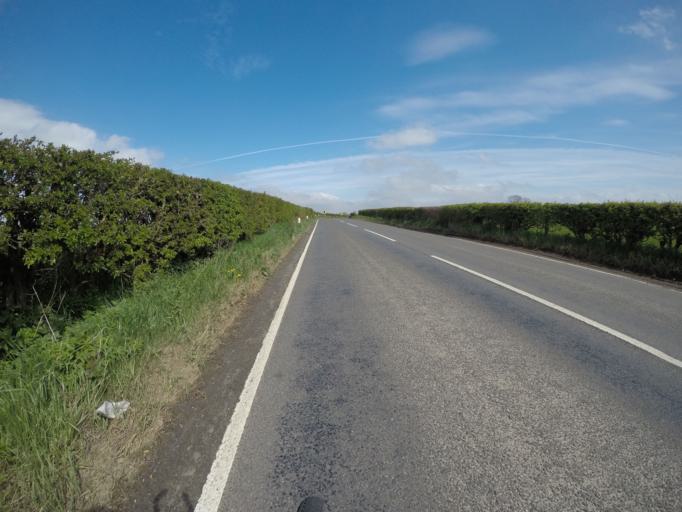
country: GB
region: Scotland
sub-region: East Ayrshire
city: Kilmaurs
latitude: 55.6650
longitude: -4.5422
